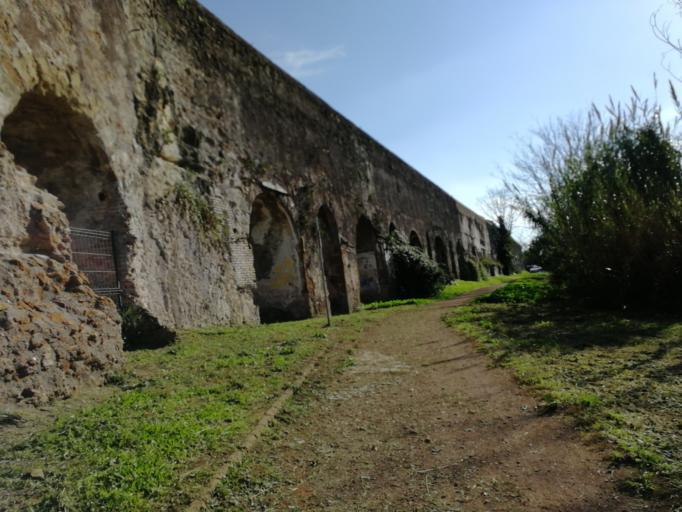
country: IT
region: Latium
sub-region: Citta metropolitana di Roma Capitale
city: Rome
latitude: 41.8585
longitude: 12.5447
